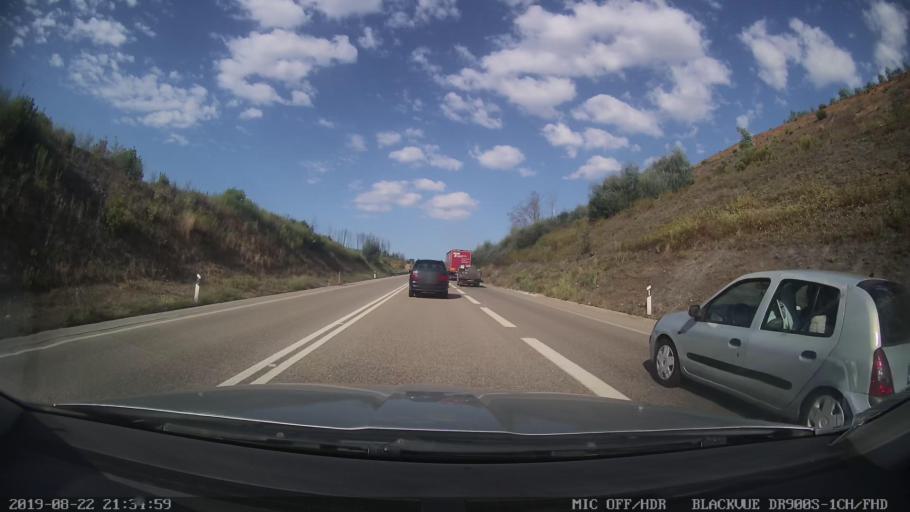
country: PT
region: Leiria
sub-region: Pedrogao Grande
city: Pedrogao Grande
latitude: 39.9257
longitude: -8.1995
